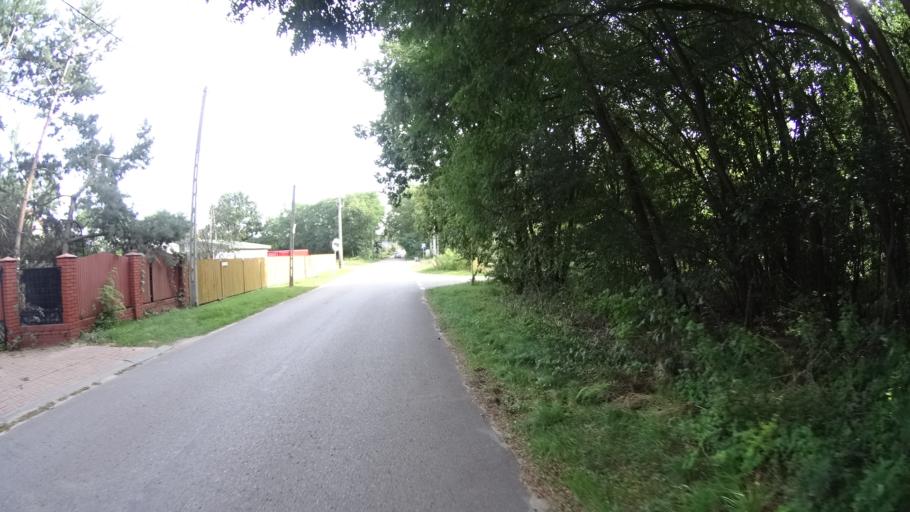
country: PL
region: Masovian Voivodeship
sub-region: Powiat legionowski
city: Serock
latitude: 52.4905
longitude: 21.0871
